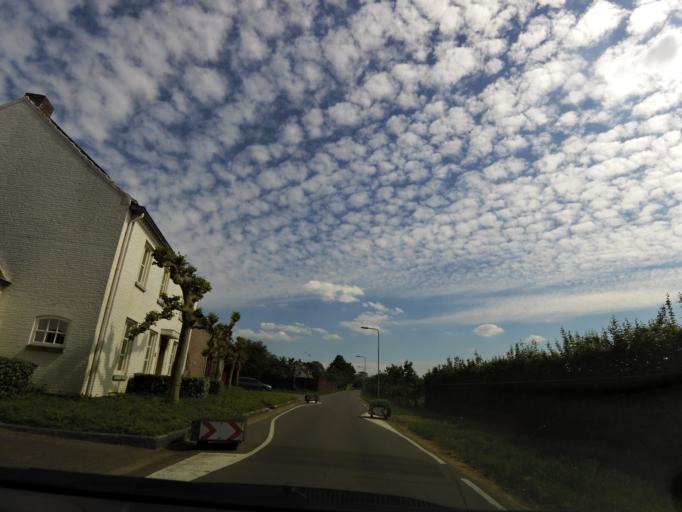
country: NL
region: Limburg
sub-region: Gemeente Roerdalen
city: Sint Odilienberg
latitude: 51.1671
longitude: 5.9897
